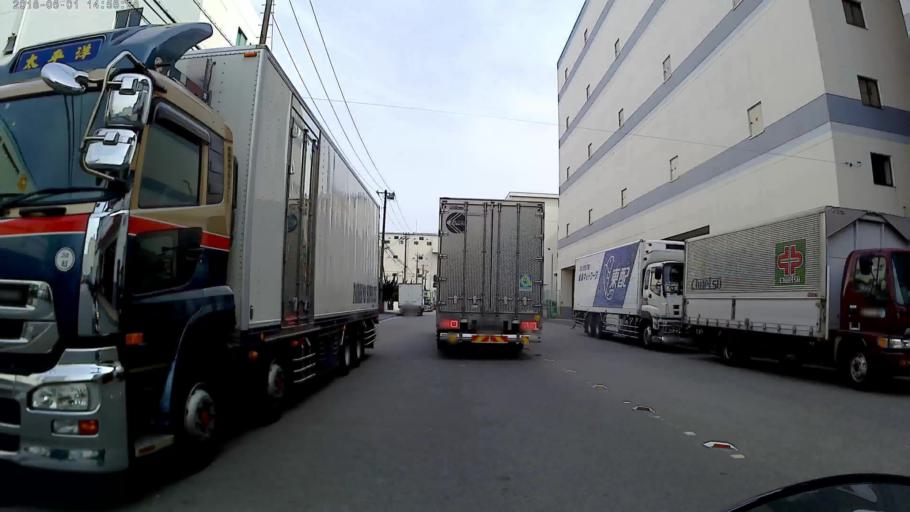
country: JP
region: Kanagawa
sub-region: Kawasaki-shi
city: Kawasaki
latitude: 35.4966
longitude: 139.7607
